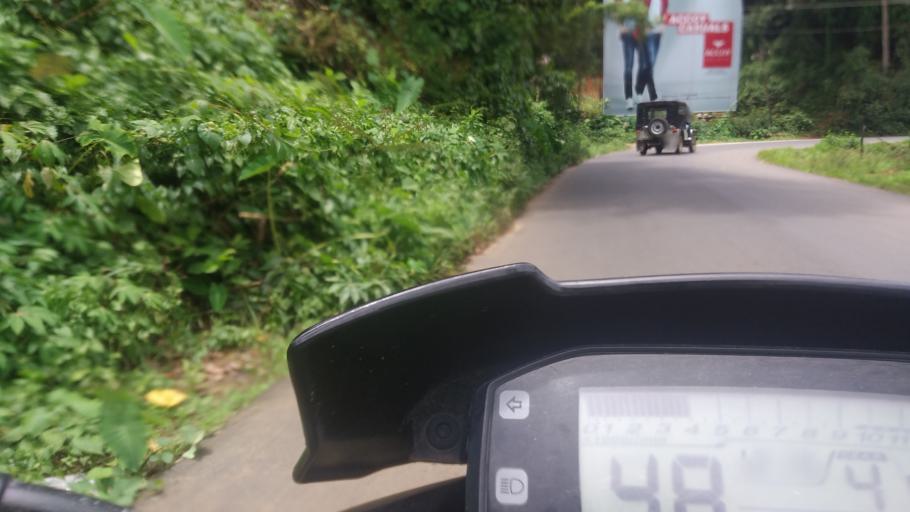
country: IN
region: Kerala
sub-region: Idukki
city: Munnar
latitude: 10.0226
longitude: 77.0004
